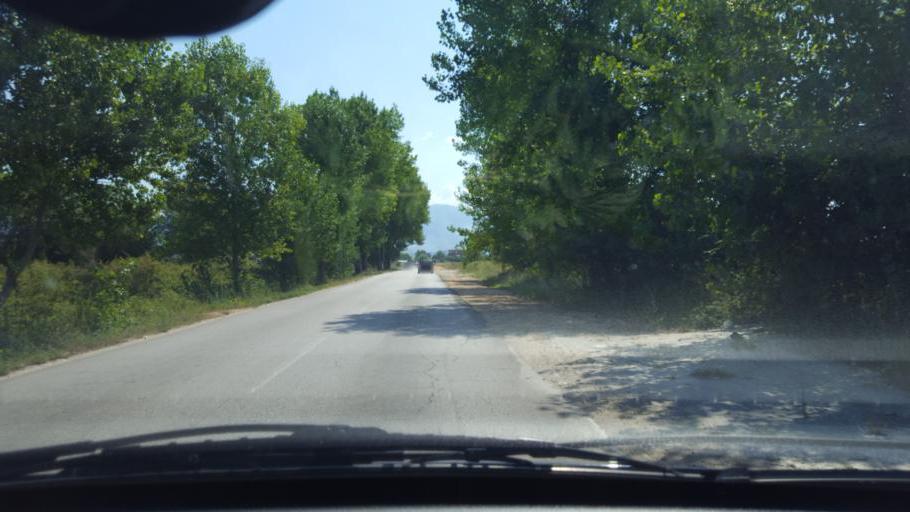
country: AL
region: Vlore
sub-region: Rrethi i Delvines
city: Finiq
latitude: 39.8795
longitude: 20.0430
